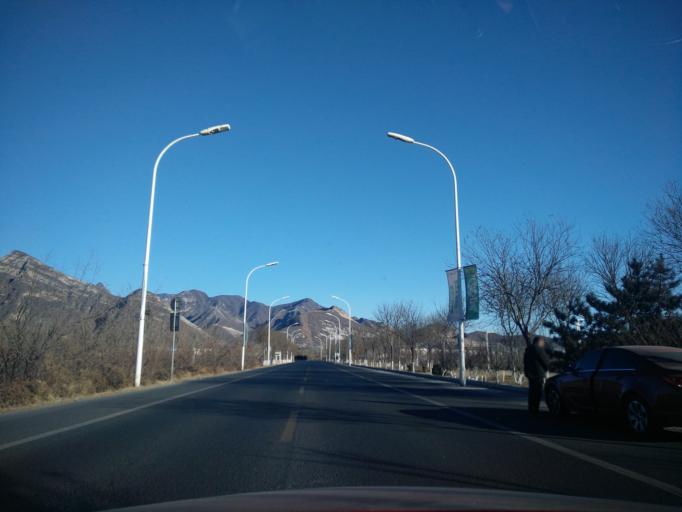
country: CN
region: Beijing
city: Junzhuang
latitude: 39.9871
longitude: 116.0808
